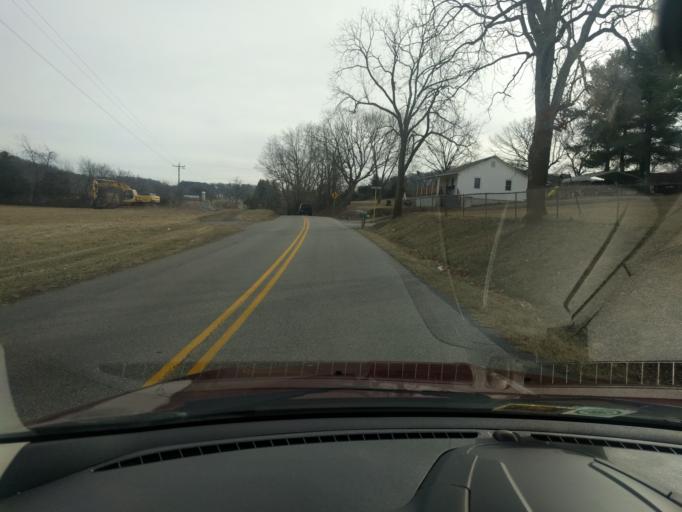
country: US
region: Virginia
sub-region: Augusta County
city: Fishersville
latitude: 38.0853
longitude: -78.9771
